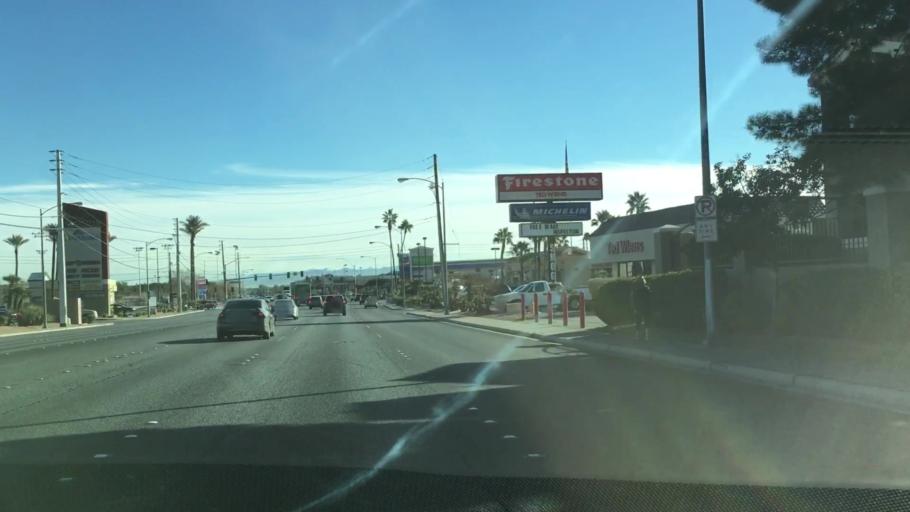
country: US
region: Nevada
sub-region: Clark County
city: Whitney
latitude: 36.0570
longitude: -115.1209
